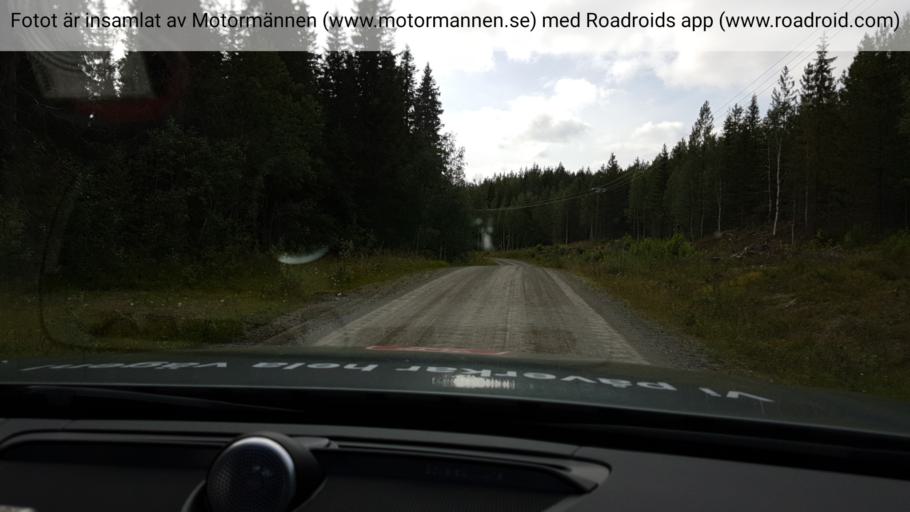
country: SE
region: Jaemtland
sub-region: Stroemsunds Kommun
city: Stroemsund
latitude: 64.5330
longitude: 15.2863
